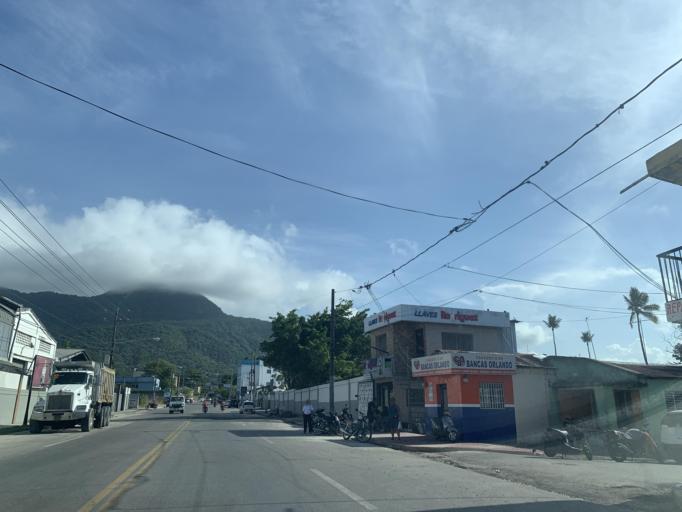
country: DO
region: Puerto Plata
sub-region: Puerto Plata
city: Puerto Plata
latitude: 19.7951
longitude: -70.6987
